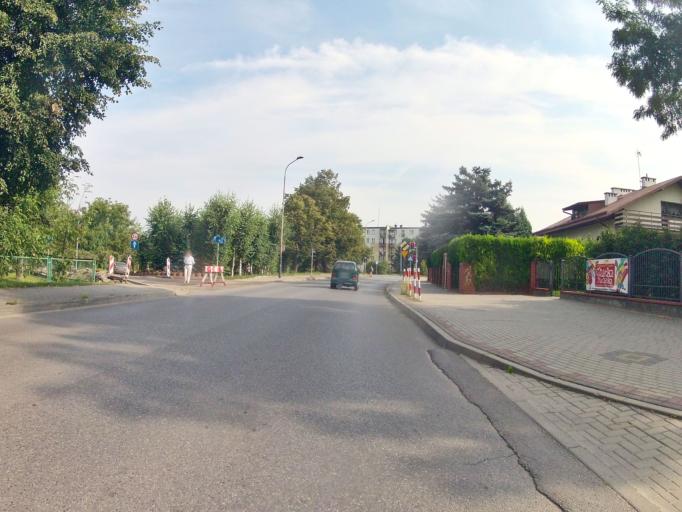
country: PL
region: Subcarpathian Voivodeship
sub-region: Powiat jasielski
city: Jaslo
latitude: 49.7475
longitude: 21.4613
